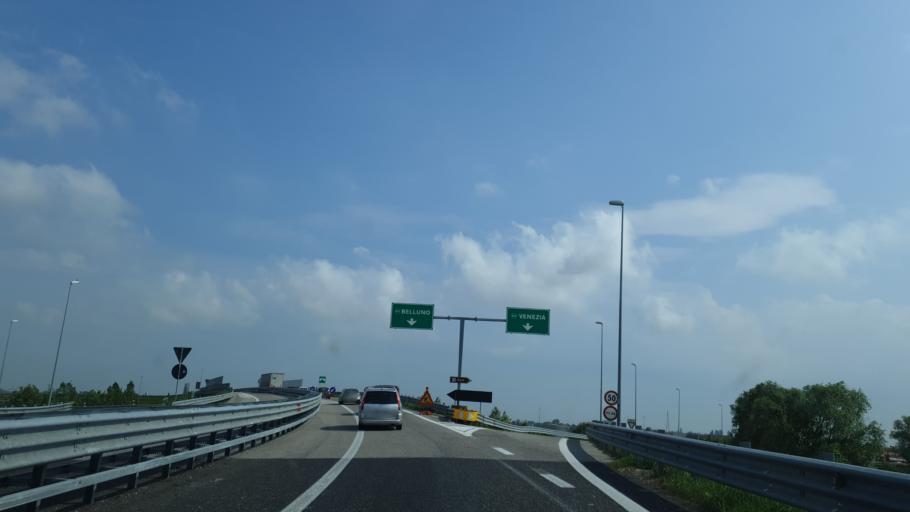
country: IT
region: Veneto
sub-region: Provincia di Venezia
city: Marcon-Gaggio-Colmello
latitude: 45.5811
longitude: 12.2886
